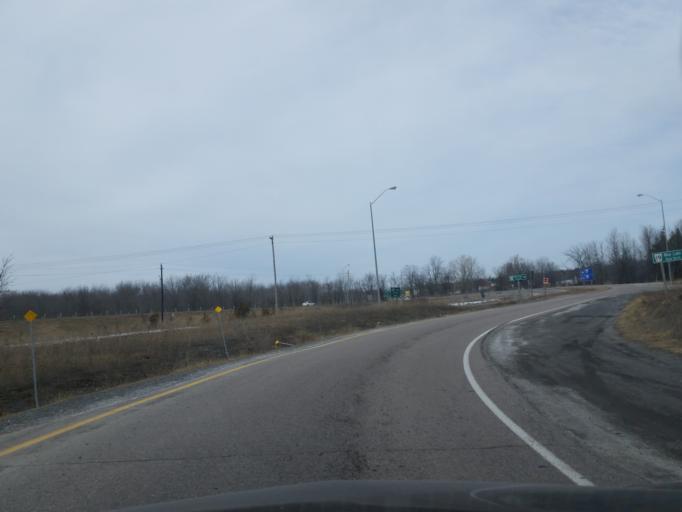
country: CA
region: Ontario
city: Skatepark
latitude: 44.2830
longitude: -76.7141
